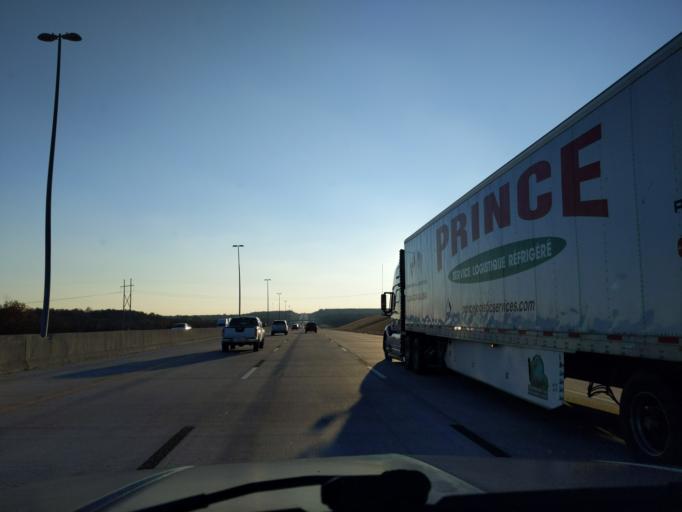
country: US
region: Oklahoma
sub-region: Creek County
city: Kellyville
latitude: 35.9737
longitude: -96.2133
